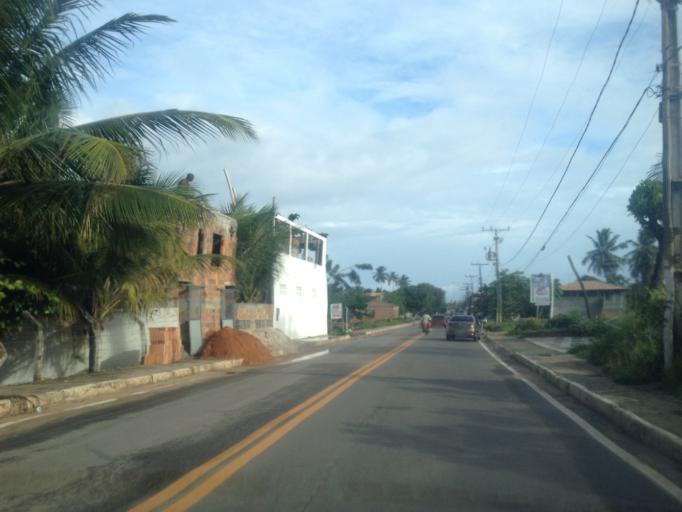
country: BR
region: Bahia
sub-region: Mata De Sao Joao
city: Mata de Sao Joao
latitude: -12.3828
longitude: -37.8815
